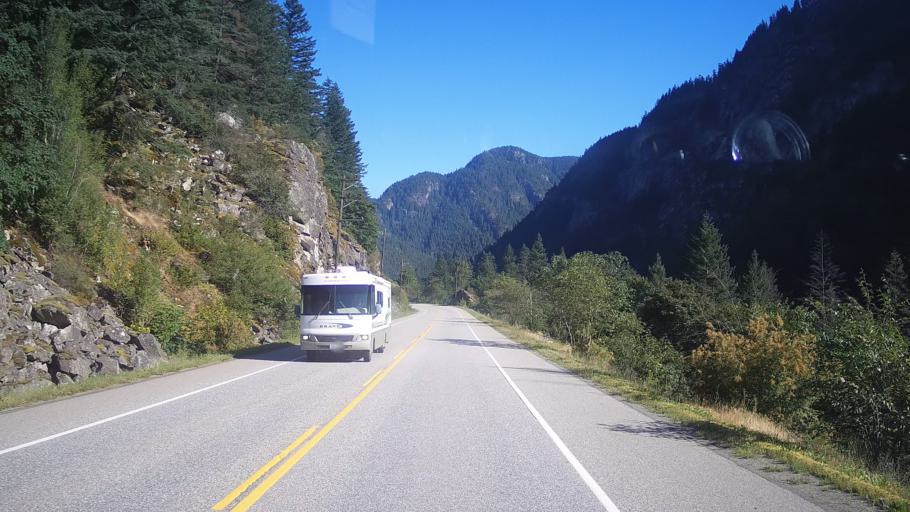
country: CA
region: British Columbia
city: Hope
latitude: 49.5850
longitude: -121.4043
